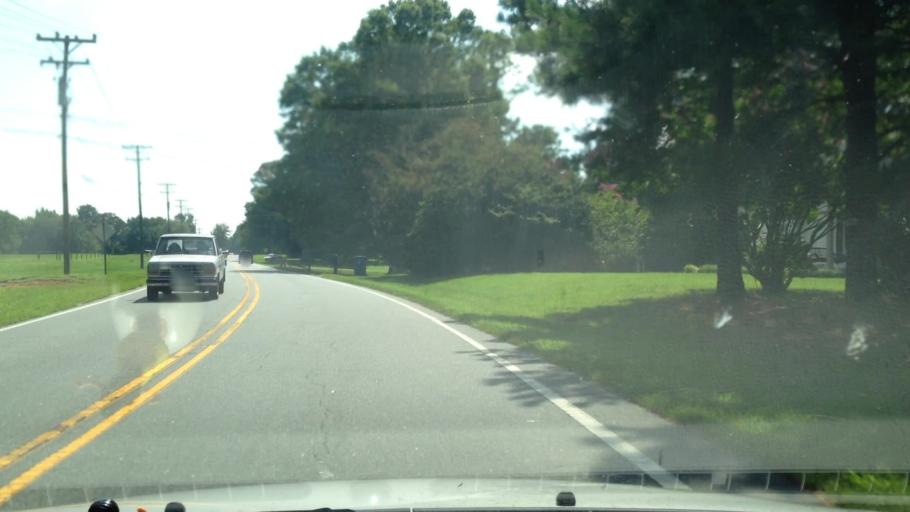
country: US
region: North Carolina
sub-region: Guilford County
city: Oak Ridge
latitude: 36.1532
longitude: -80.0348
